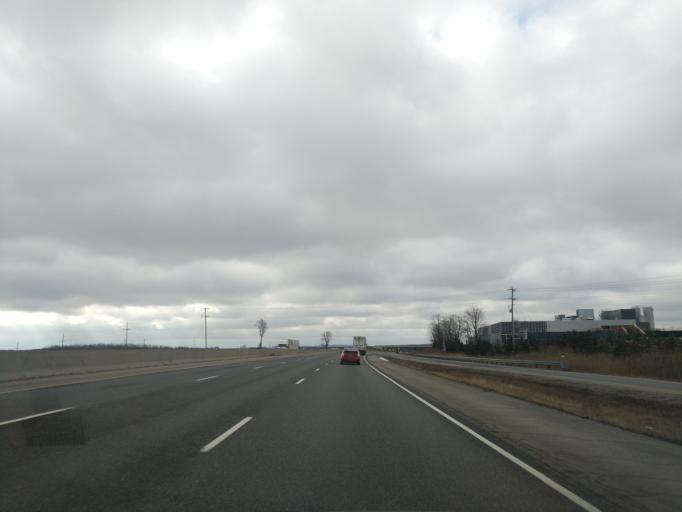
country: CA
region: Ontario
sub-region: Oxford County
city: Woodstock
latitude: 43.1313
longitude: -80.6868
